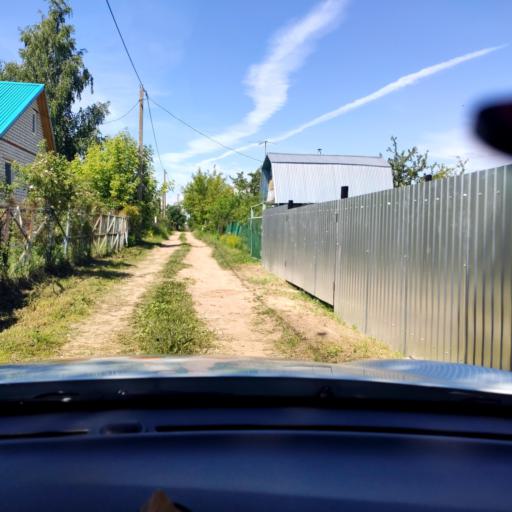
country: RU
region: Tatarstan
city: Vysokaya Gora
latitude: 55.8122
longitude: 49.2877
